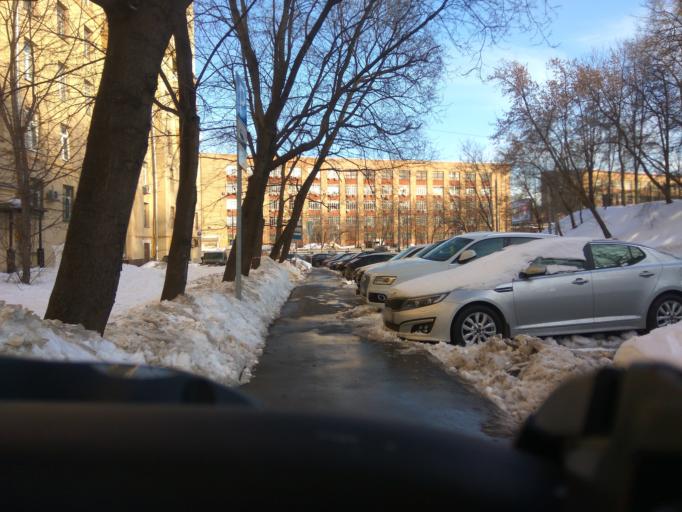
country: RU
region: Moscow
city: Lefortovo
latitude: 55.7889
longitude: 37.6975
